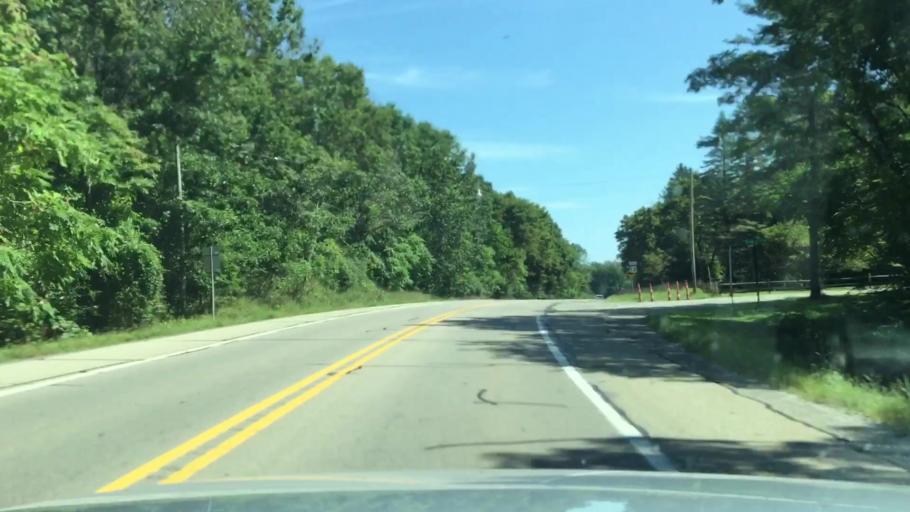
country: US
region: Michigan
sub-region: Washtenaw County
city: Manchester
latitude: 42.0610
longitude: -84.1229
